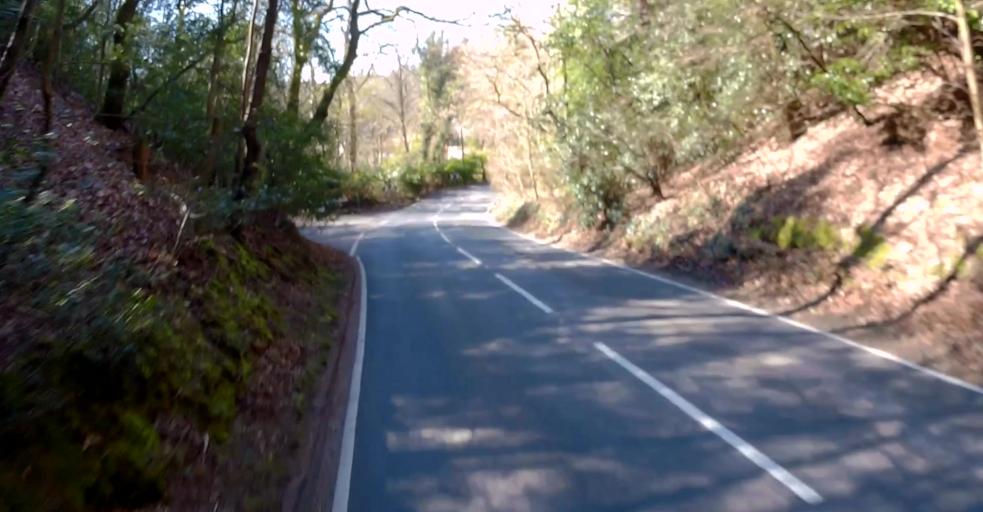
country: GB
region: England
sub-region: Surrey
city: Farnham
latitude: 51.2014
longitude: -0.7767
